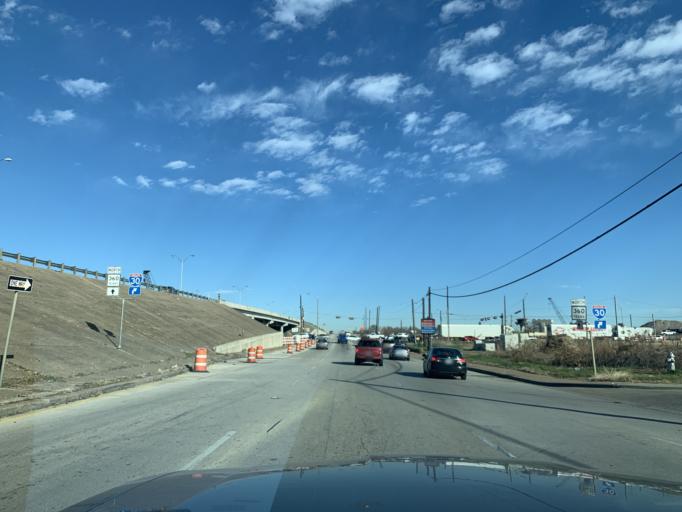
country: US
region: Texas
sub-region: Tarrant County
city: Arlington
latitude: 32.7565
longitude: -97.0630
